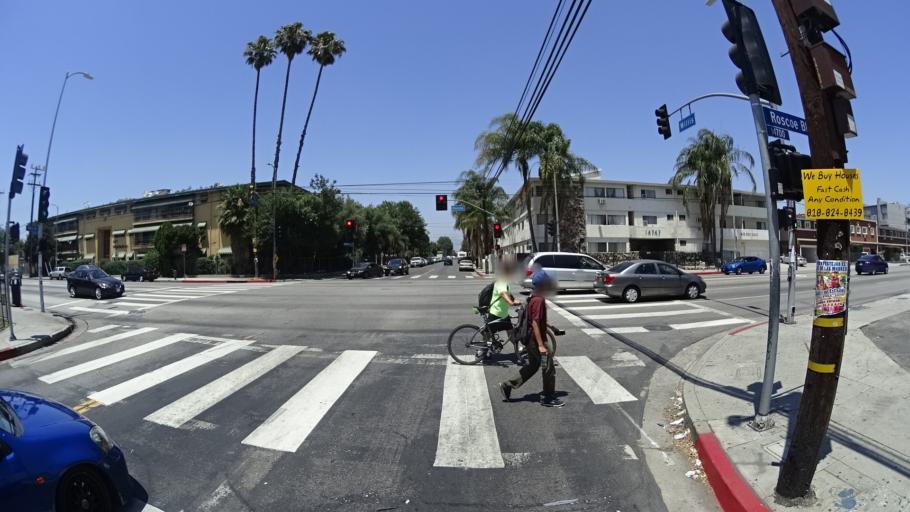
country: US
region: California
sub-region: Los Angeles County
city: Van Nuys
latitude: 34.2213
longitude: -118.4554
